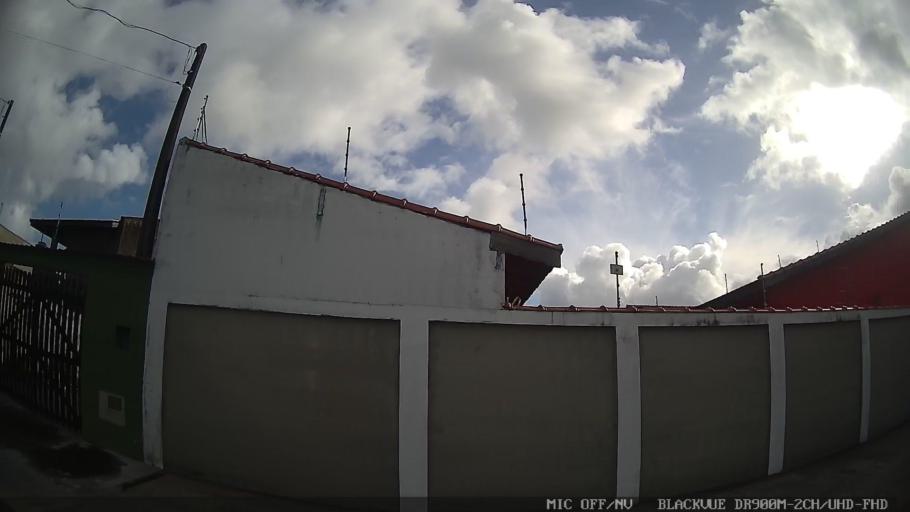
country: BR
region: Sao Paulo
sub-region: Itanhaem
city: Itanhaem
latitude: -24.1933
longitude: -46.8257
